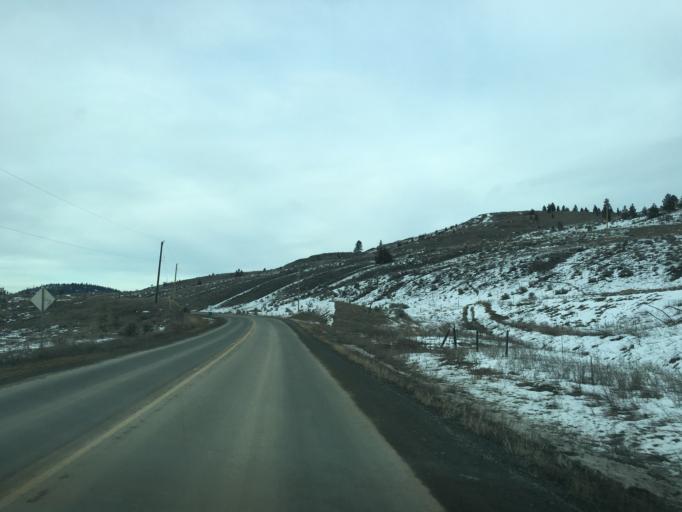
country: CA
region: British Columbia
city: Kamloops
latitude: 50.6180
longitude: -120.4430
